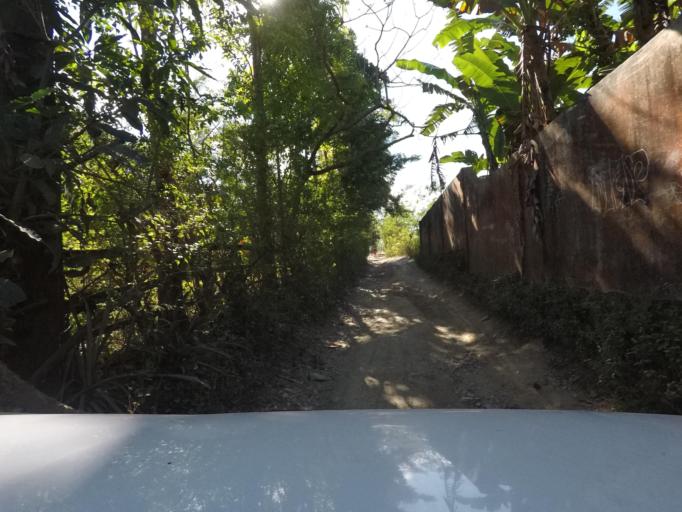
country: TL
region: Ermera
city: Gleno
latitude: -8.7117
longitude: 125.4477
